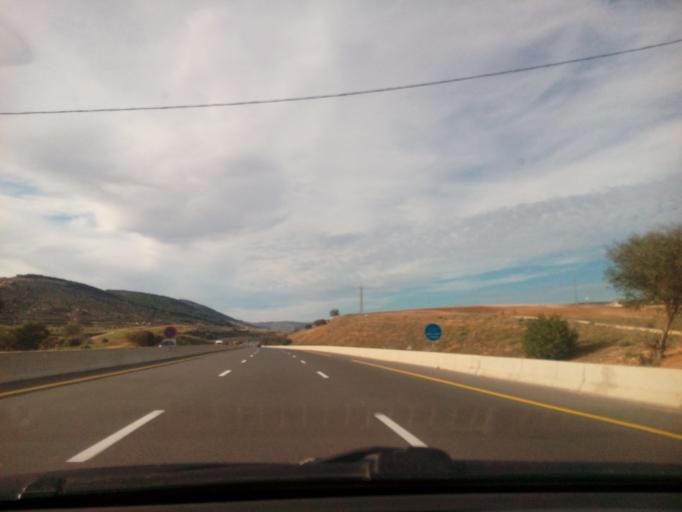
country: DZ
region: Sidi Bel Abbes
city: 'Ain el Berd
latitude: 35.4421
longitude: -0.4170
